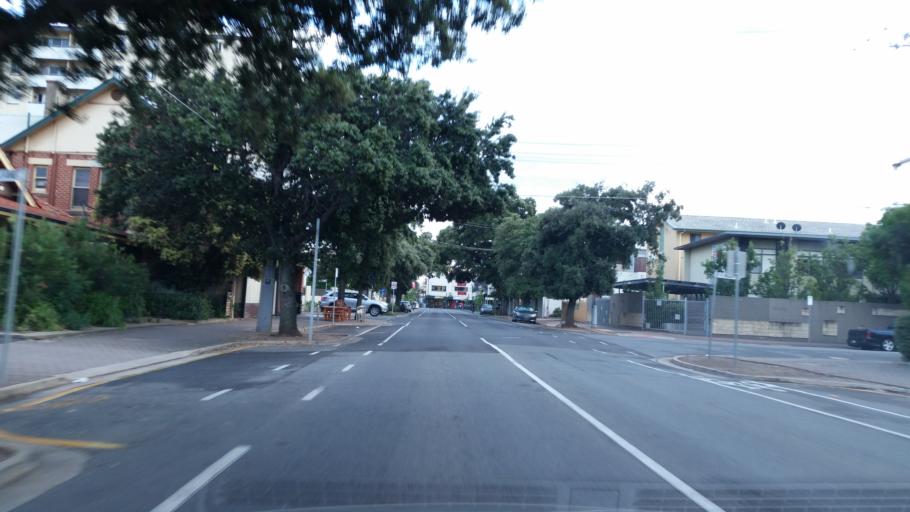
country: AU
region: South Australia
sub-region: Adelaide
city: Glenelg
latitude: -34.9822
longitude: 138.5132
